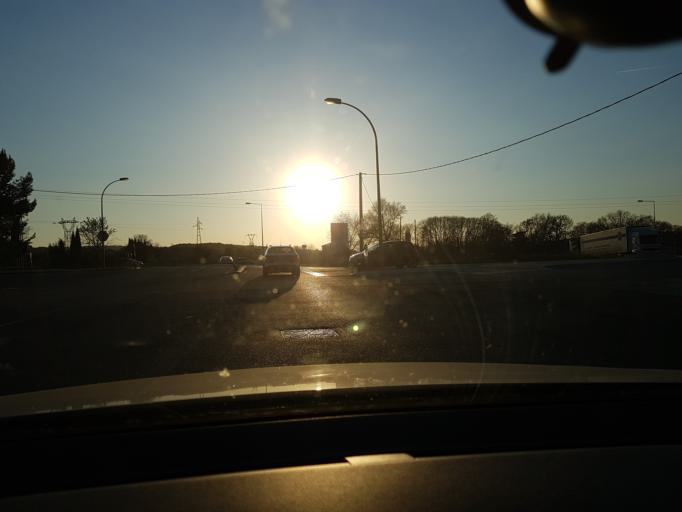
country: FR
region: Provence-Alpes-Cote d'Azur
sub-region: Departement des Bouches-du-Rhone
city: Rousset
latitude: 43.4709
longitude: 5.5970
